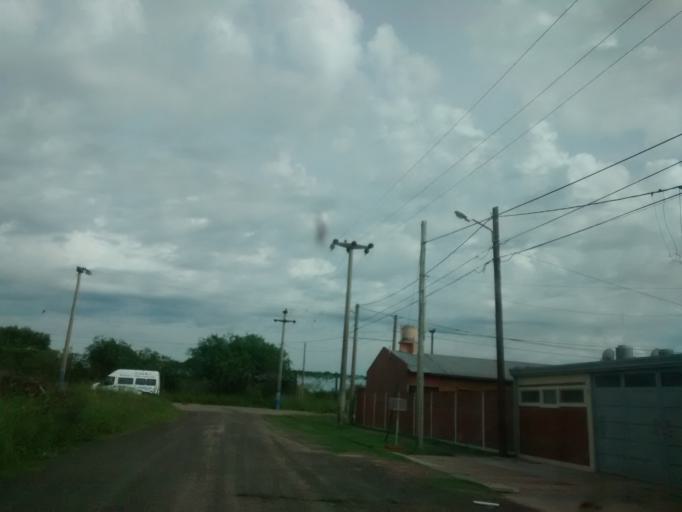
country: AR
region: Chaco
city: Resistencia
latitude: -27.4135
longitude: -58.9643
